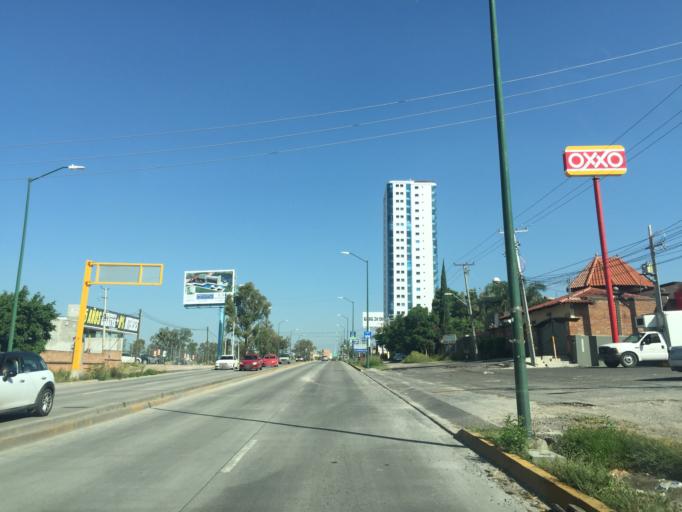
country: MX
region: Guanajuato
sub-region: Leon
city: La Ermita
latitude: 21.1572
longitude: -101.7215
